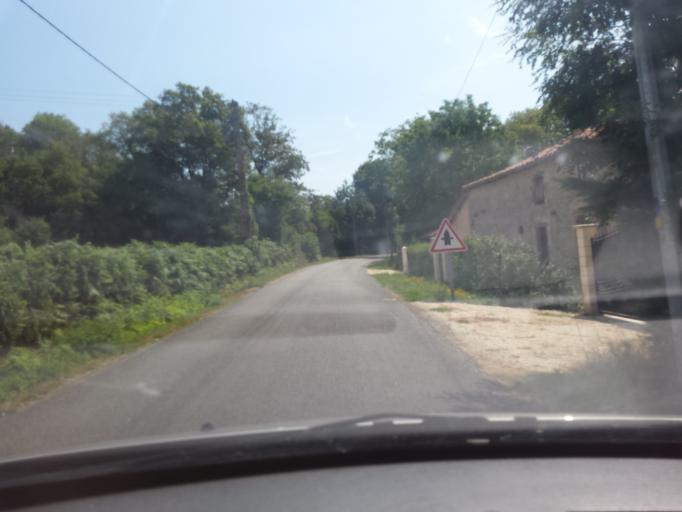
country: FR
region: Poitou-Charentes
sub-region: Departement de la Vienne
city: Availles-Limouzine
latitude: 46.1082
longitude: 0.6838
